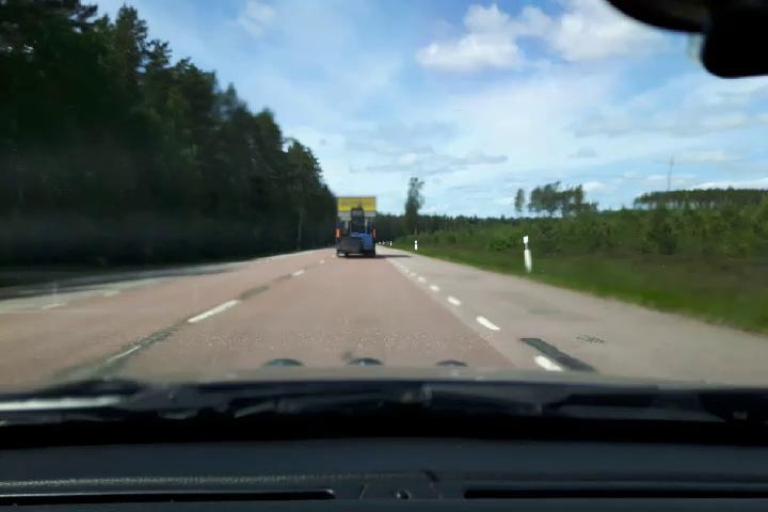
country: SE
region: Uppsala
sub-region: Osthammars Kommun
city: Bjorklinge
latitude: 60.1179
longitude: 17.5158
